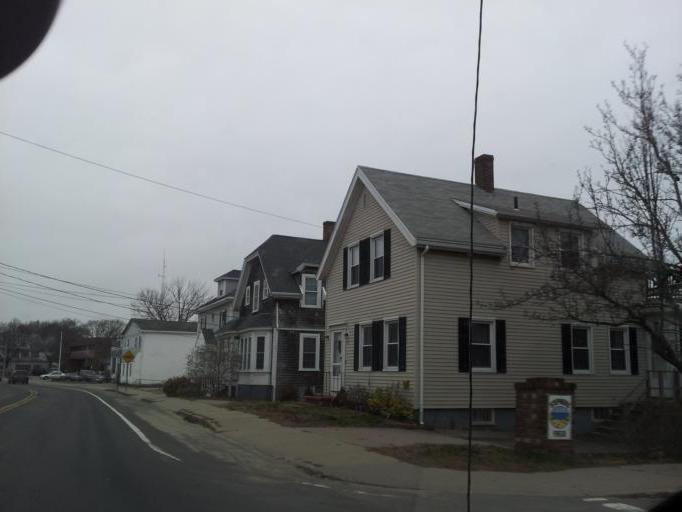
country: US
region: Massachusetts
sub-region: Plymouth County
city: Plymouth
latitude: 41.9515
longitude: -70.6558
